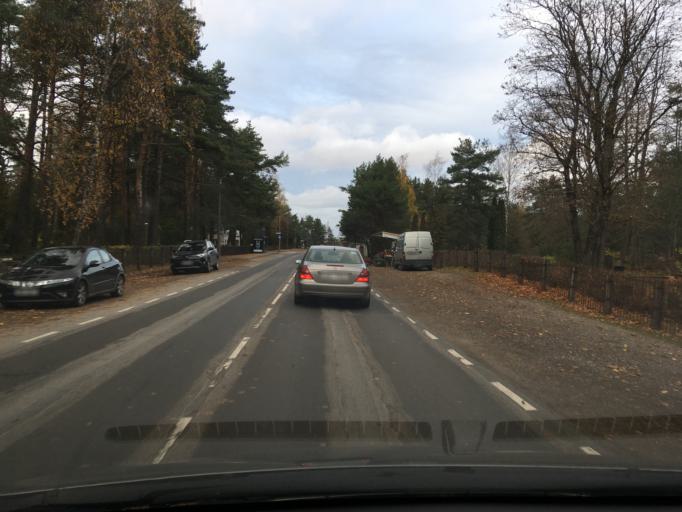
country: EE
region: Harju
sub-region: Tallinna linn
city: Tallinn
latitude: 59.3912
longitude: 24.7087
